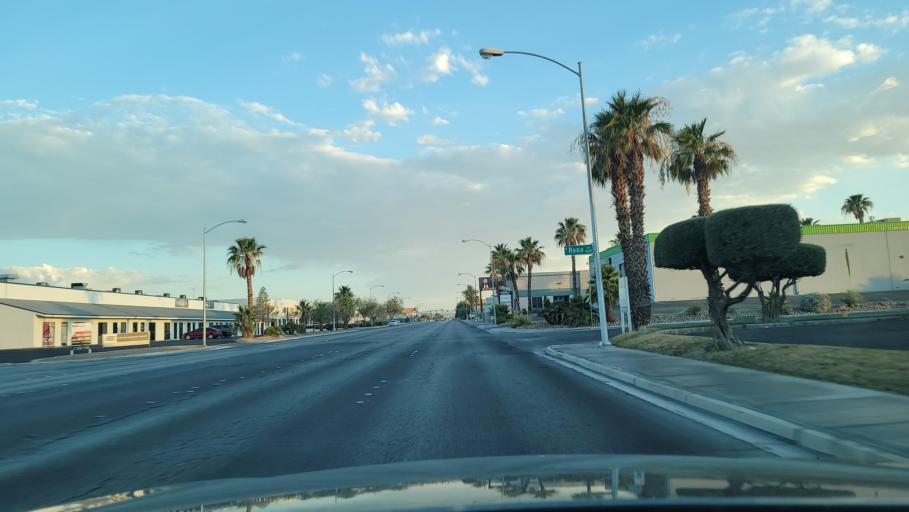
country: US
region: Nevada
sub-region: Clark County
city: Spring Valley
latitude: 36.0977
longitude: -115.1993
